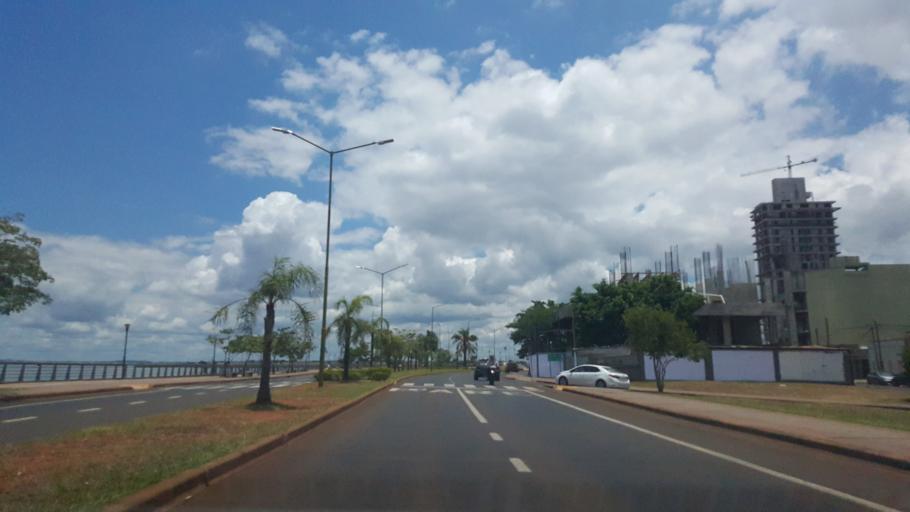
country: AR
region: Misiones
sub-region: Departamento de Capital
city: Posadas
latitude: -27.3667
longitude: -55.8845
